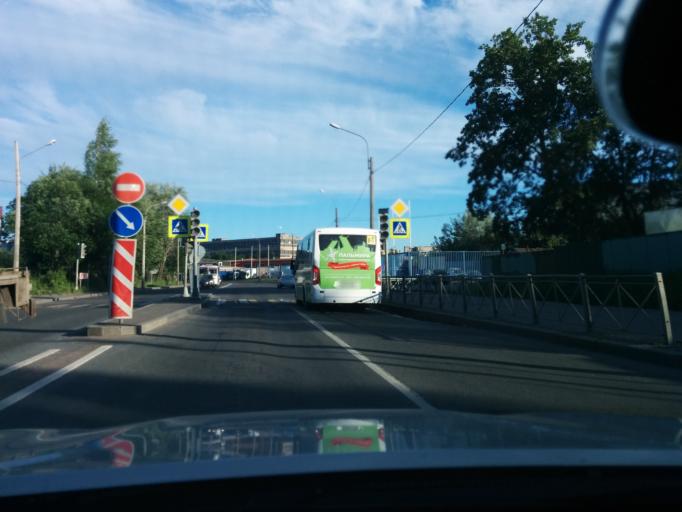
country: RU
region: Leningrad
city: Finlyandskiy
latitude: 59.9780
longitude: 30.3672
